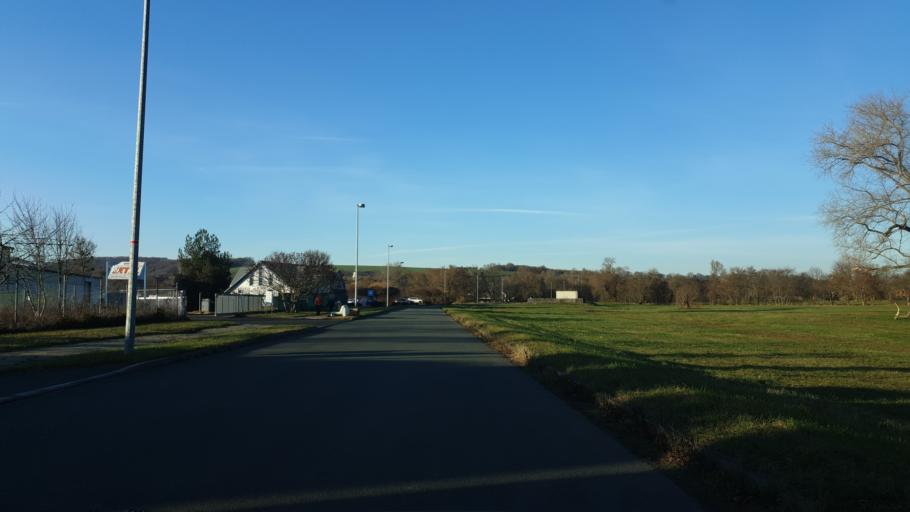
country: DE
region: Thuringia
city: Hartmannsdorf
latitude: 50.9694
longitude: 11.9865
